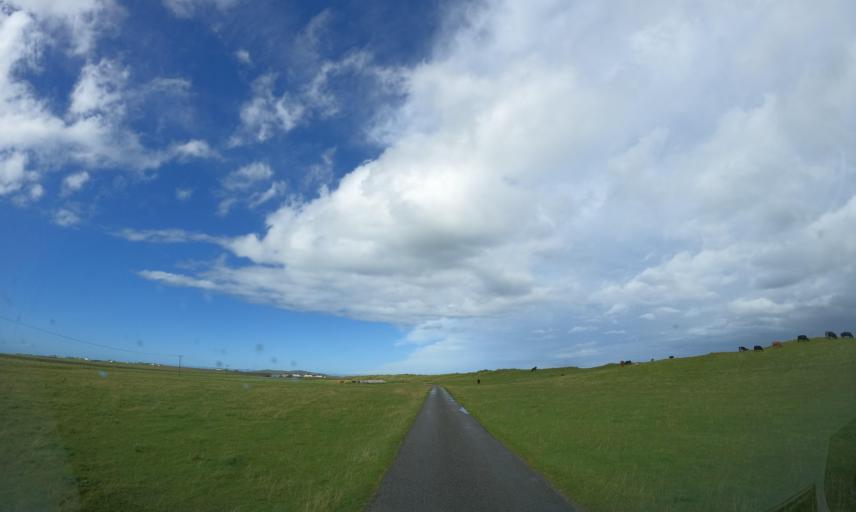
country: GB
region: Scotland
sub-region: Eilean Siar
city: Barra
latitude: 56.5186
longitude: -6.8685
